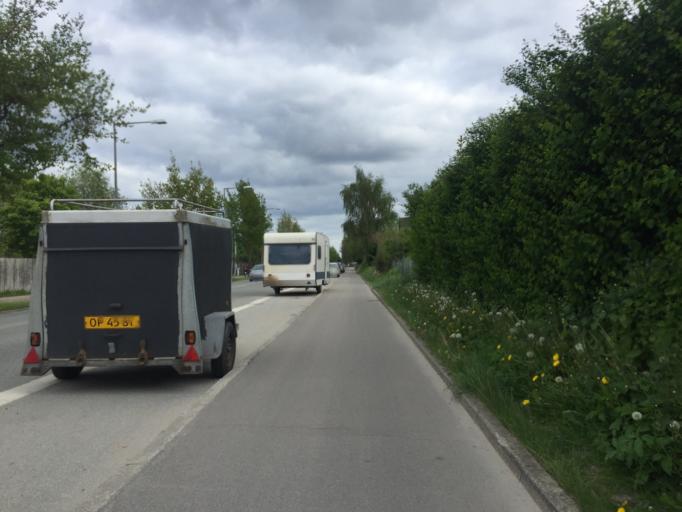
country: DK
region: Capital Region
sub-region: Kobenhavn
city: Christianshavn
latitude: 55.6804
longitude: 12.6159
